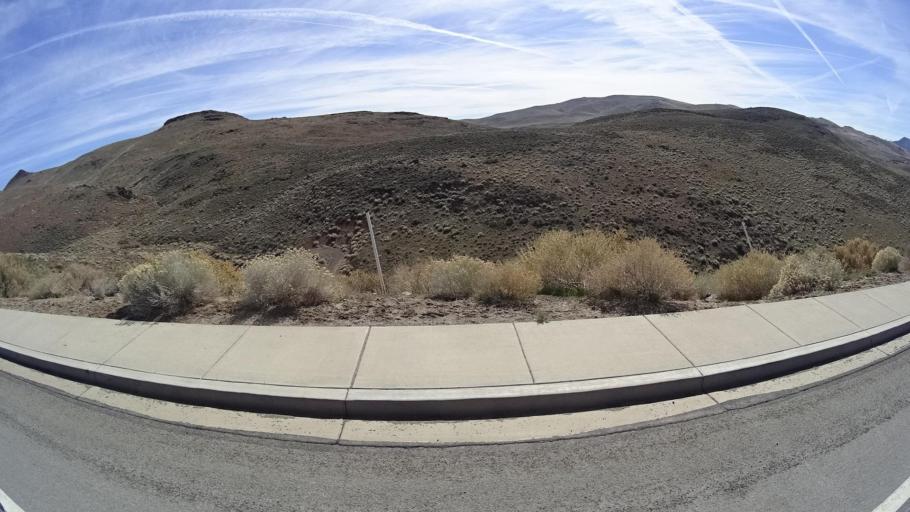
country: US
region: Nevada
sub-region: Washoe County
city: Spanish Springs
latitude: 39.5762
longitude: -119.6892
